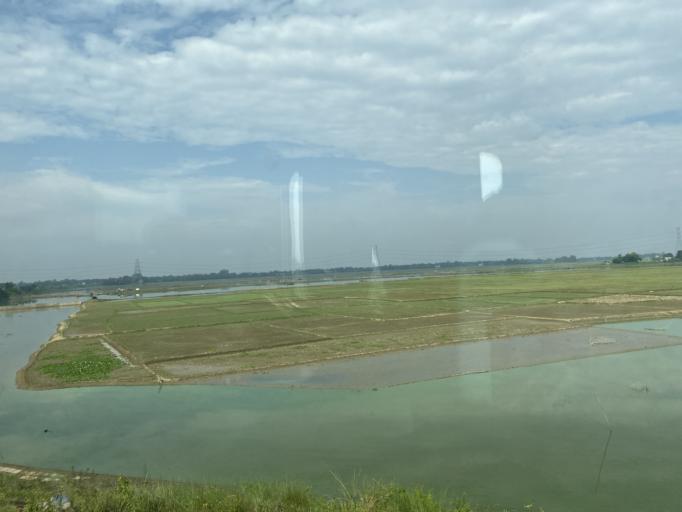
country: IN
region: Tripura
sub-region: West Tripura
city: Agartala
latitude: 23.8803
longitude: 91.2038
